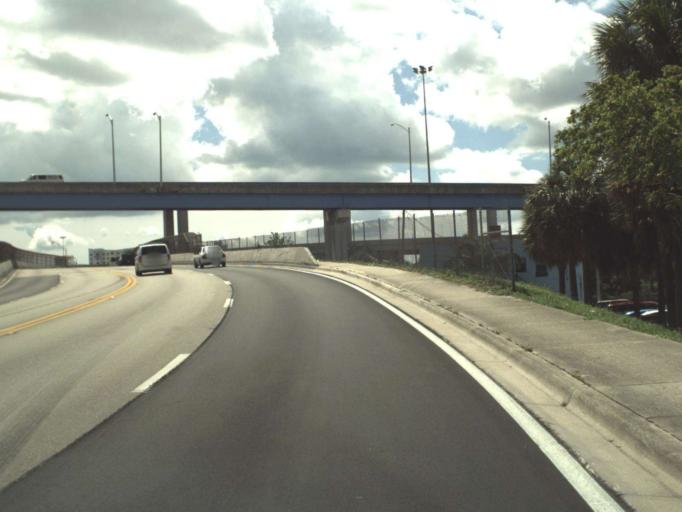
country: US
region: Florida
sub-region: Miami-Dade County
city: Allapattah
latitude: 25.8149
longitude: -80.2077
